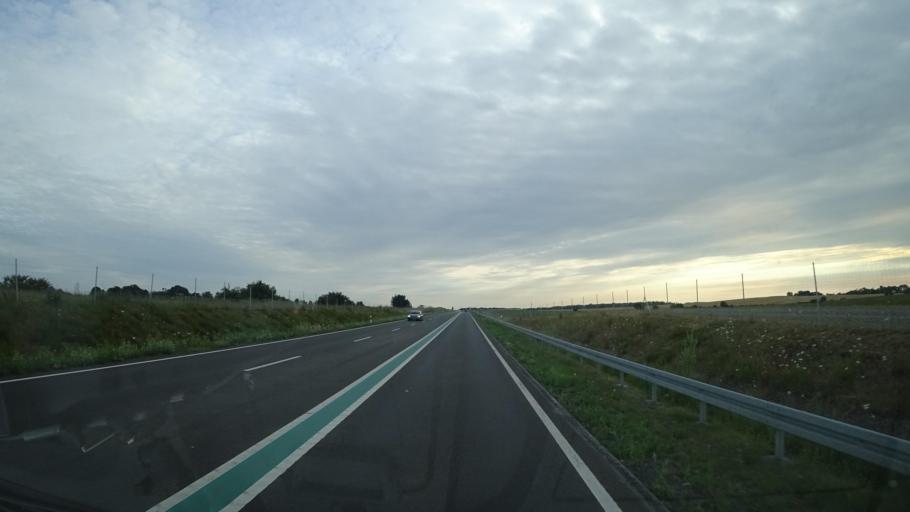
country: DE
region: Mecklenburg-Vorpommern
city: Samtens
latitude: 54.3716
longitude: 13.3296
